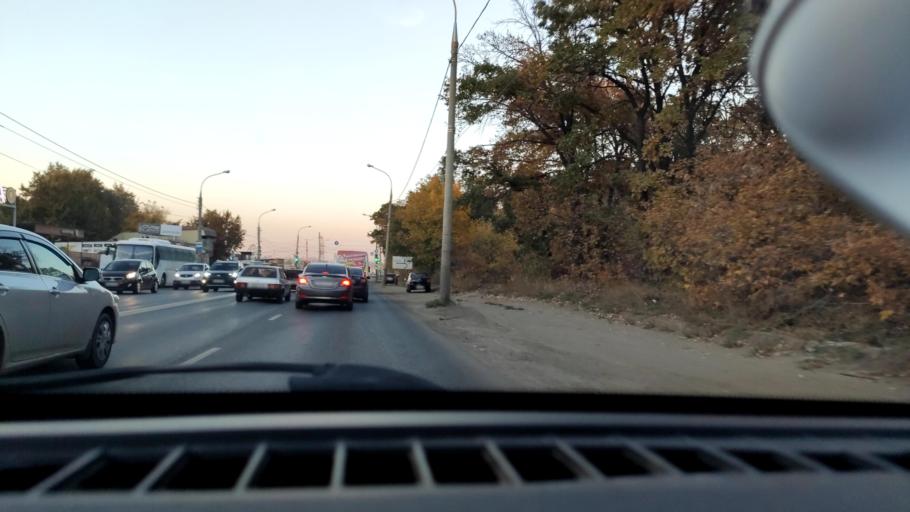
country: RU
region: Samara
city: Samara
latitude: 53.1298
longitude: 50.1720
